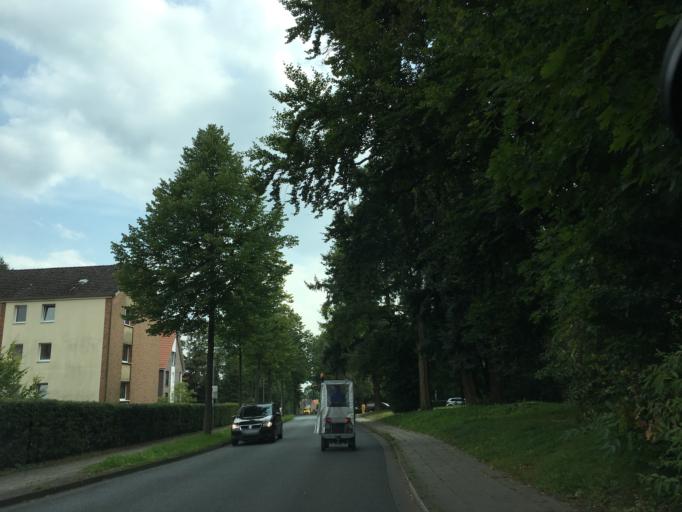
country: DE
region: Lower Saxony
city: Lueneburg
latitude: 53.2565
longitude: 10.3867
